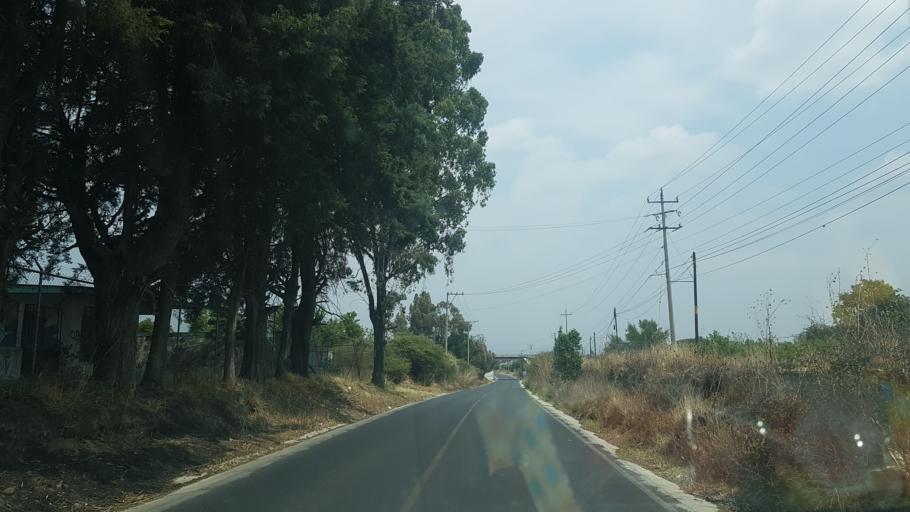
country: MX
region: Puebla
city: Huejotzingo
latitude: 19.1414
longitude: -98.4120
